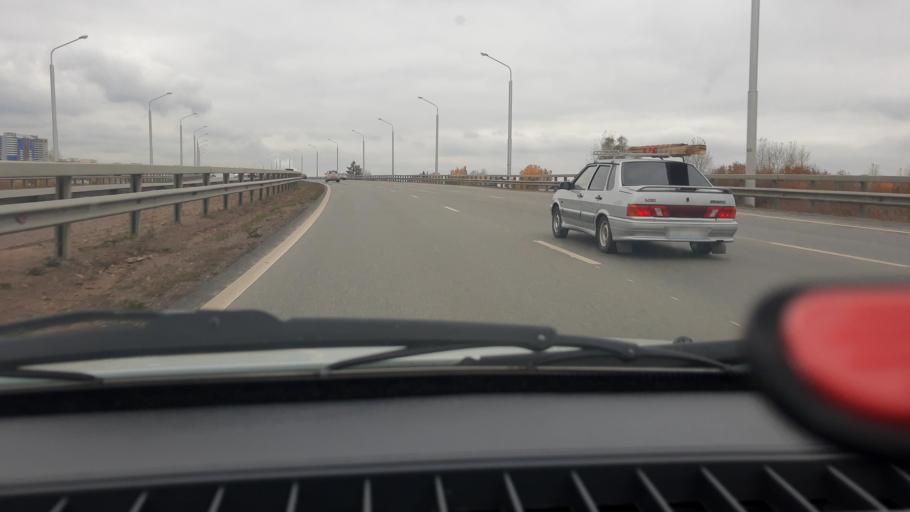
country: RU
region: Bashkortostan
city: Mikhaylovka
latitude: 54.7976
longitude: 55.8980
